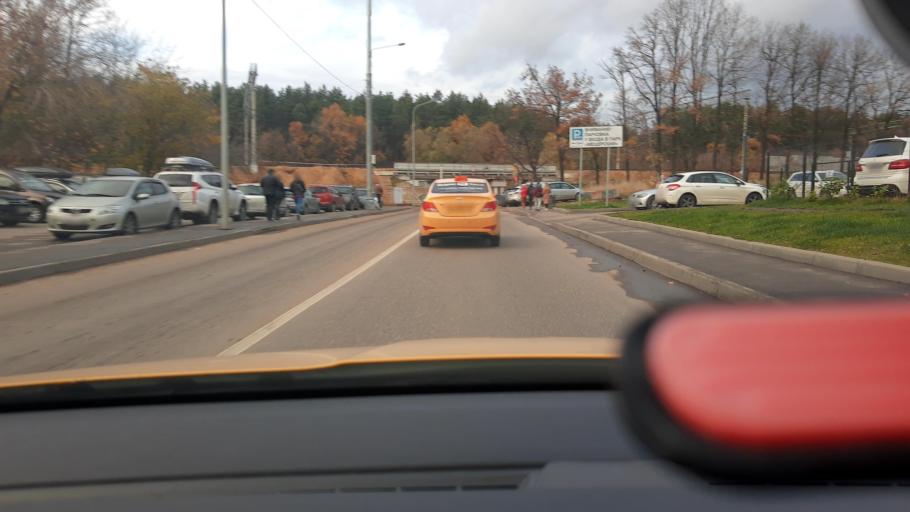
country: RU
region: Moskovskaya
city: Zarech'ye
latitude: 55.6614
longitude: 37.4085
